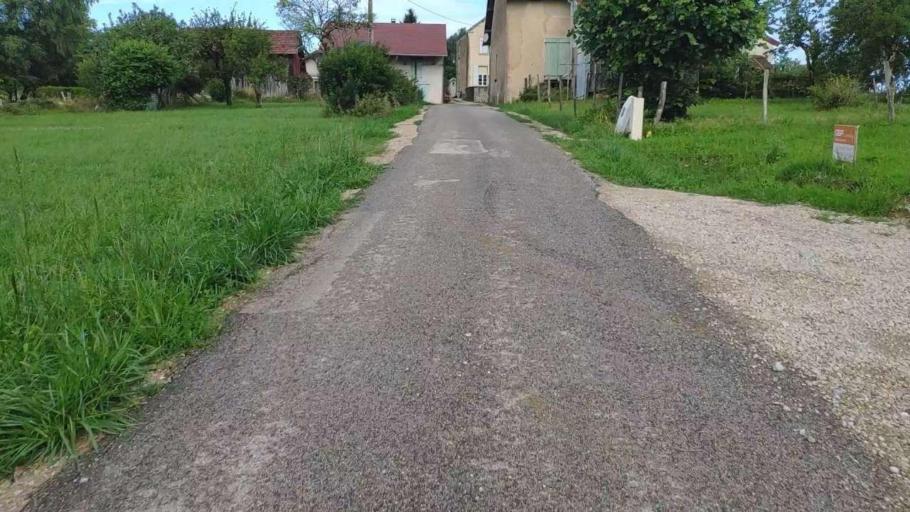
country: FR
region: Franche-Comte
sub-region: Departement du Jura
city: Poligny
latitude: 46.8018
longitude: 5.5908
